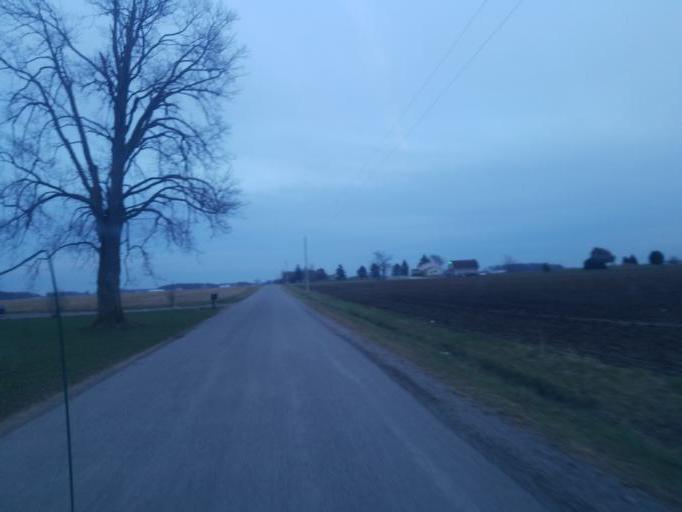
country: US
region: Indiana
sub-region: Adams County
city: Decatur
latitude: 40.7583
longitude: -85.0138
